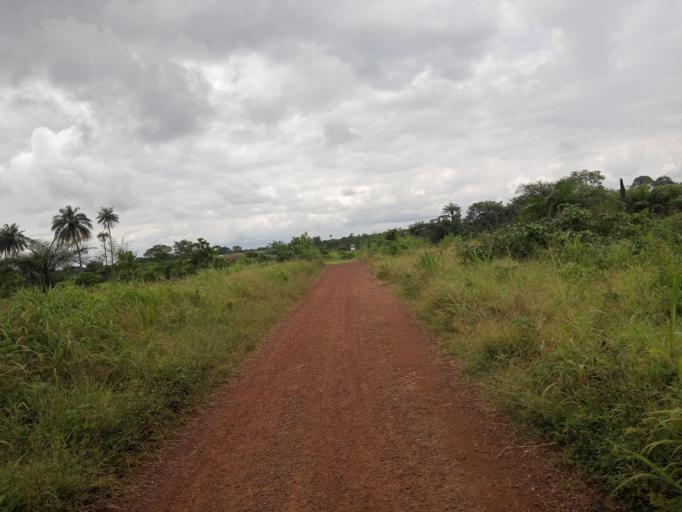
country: SL
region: Northern Province
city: Kamakwie
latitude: 9.4858
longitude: -12.2468
